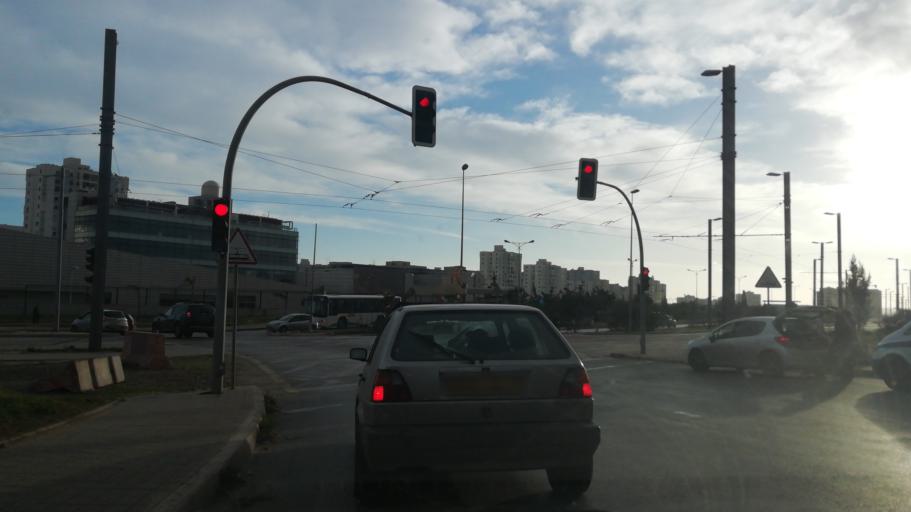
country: DZ
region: Oran
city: Bir el Djir
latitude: 35.7066
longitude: -0.5724
